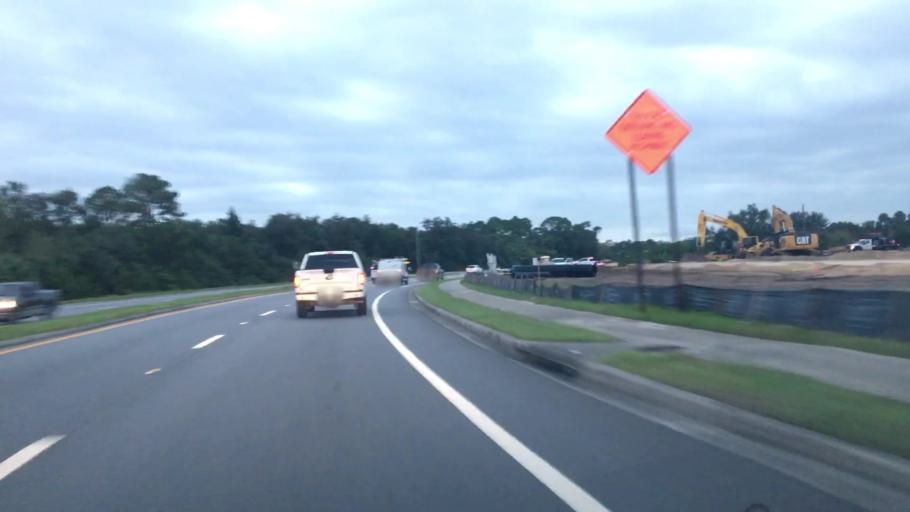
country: US
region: Florida
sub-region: Seminole County
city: Midway
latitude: 28.7819
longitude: -81.2114
